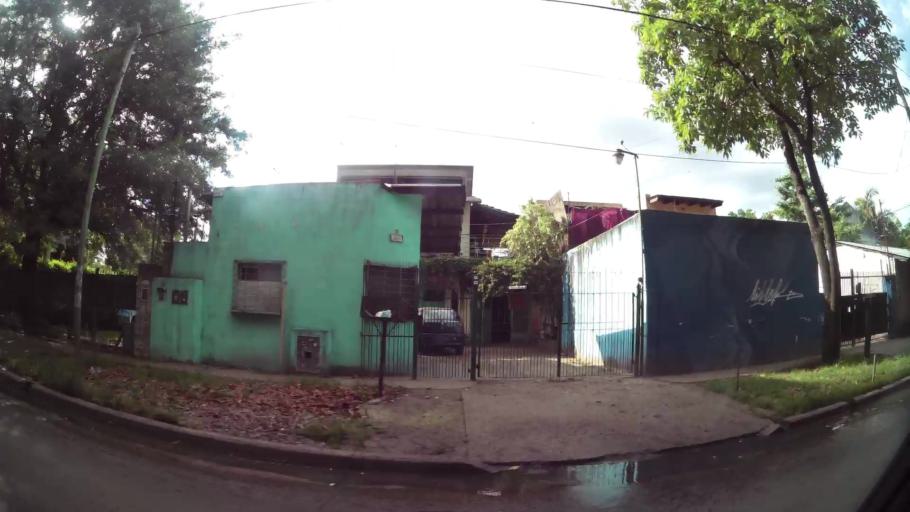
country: AR
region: Buenos Aires
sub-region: Partido de Tigre
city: Tigre
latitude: -34.4709
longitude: -58.6598
